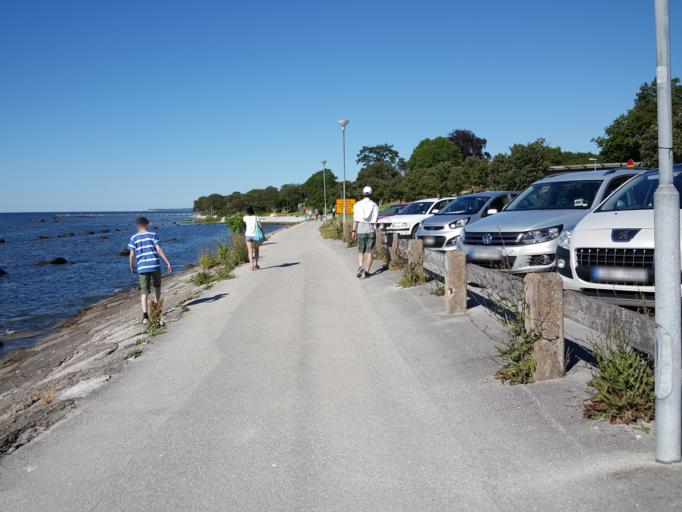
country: SE
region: Gotland
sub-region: Gotland
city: Visby
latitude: 57.6496
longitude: 18.2994
